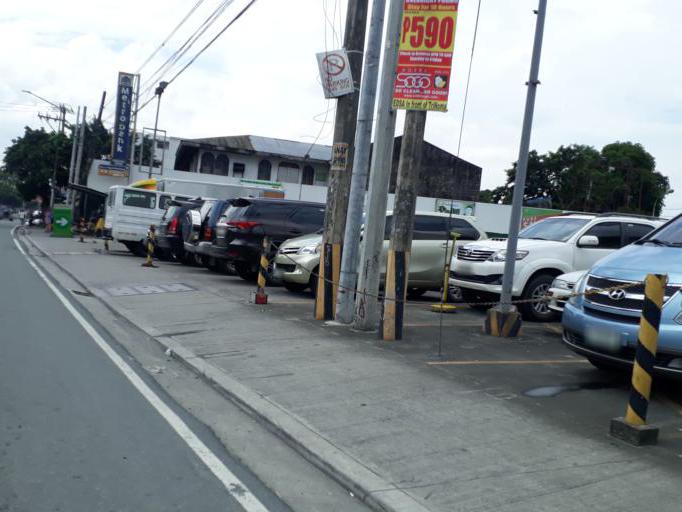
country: PH
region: Calabarzon
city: Bagong Pagasa
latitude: 14.6667
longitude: 121.0349
